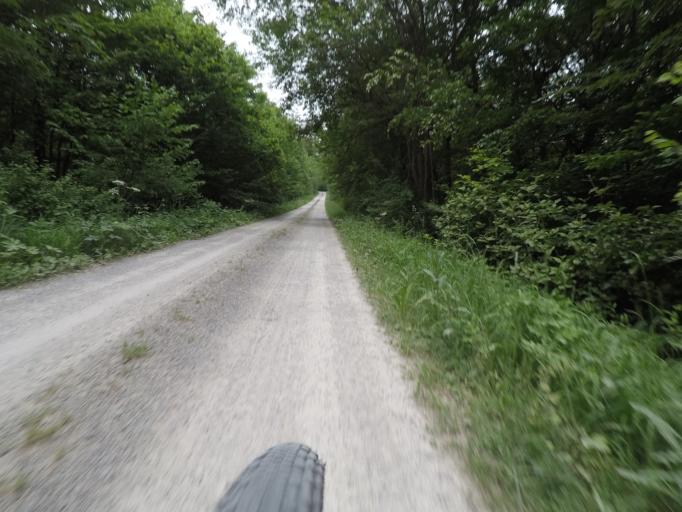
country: DE
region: Baden-Wuerttemberg
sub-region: Regierungsbezirk Stuttgart
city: Hildrizhausen
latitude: 48.5749
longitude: 8.9762
